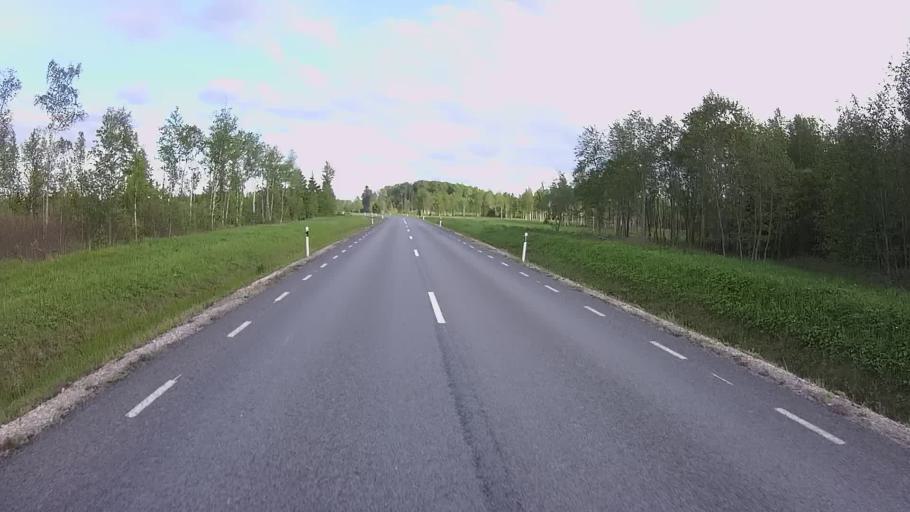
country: EE
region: Jogevamaa
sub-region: Mustvee linn
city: Mustvee
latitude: 59.0565
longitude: 27.0106
